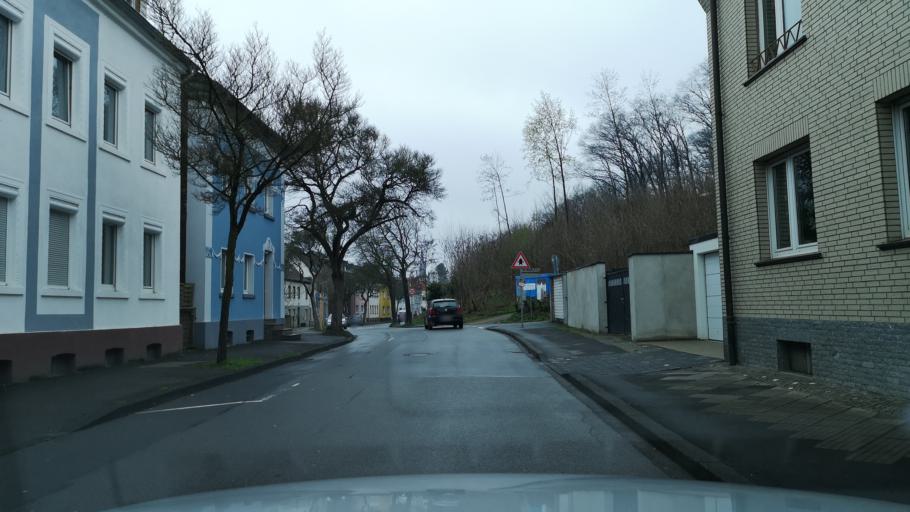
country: DE
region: North Rhine-Westphalia
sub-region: Regierungsbezirk Arnsberg
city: Menden
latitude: 51.4341
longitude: 7.8046
